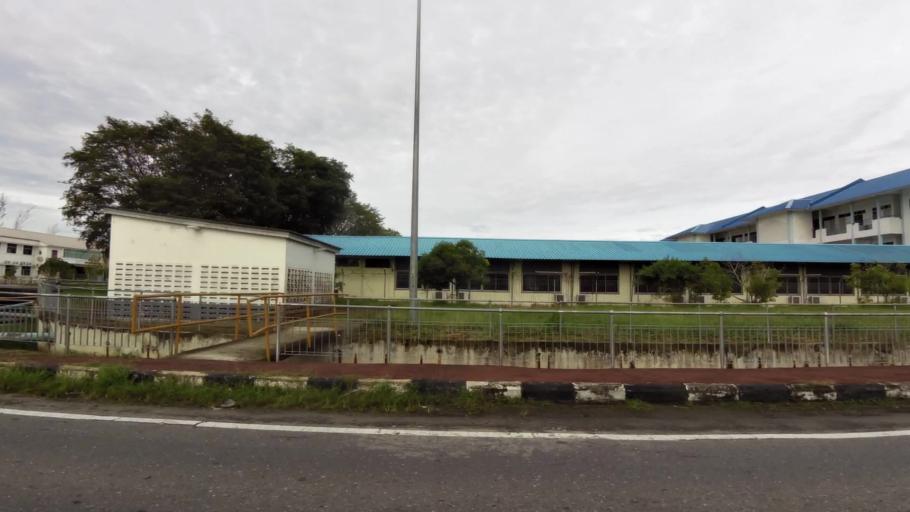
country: BN
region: Belait
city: Seria
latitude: 4.6100
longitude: 114.3360
